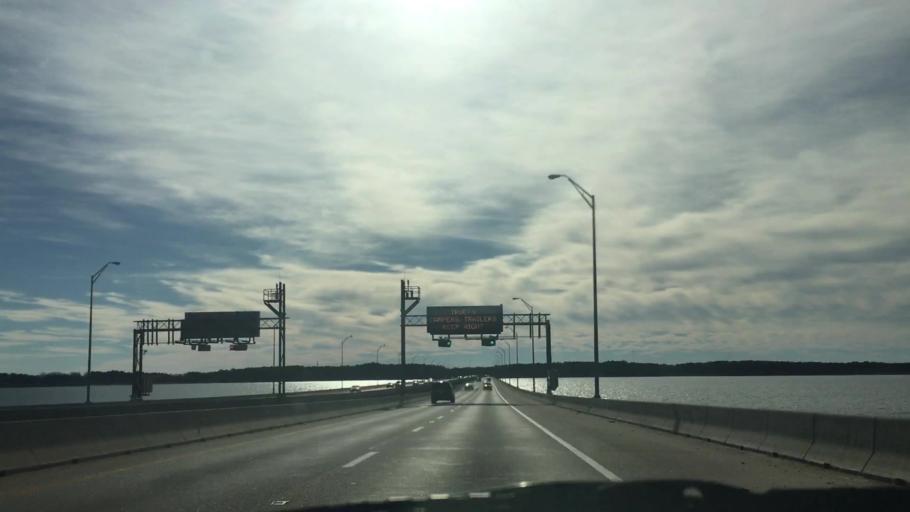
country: US
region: Virginia
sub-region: City of Newport News
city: Newport News
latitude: 36.9133
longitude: -76.4126
